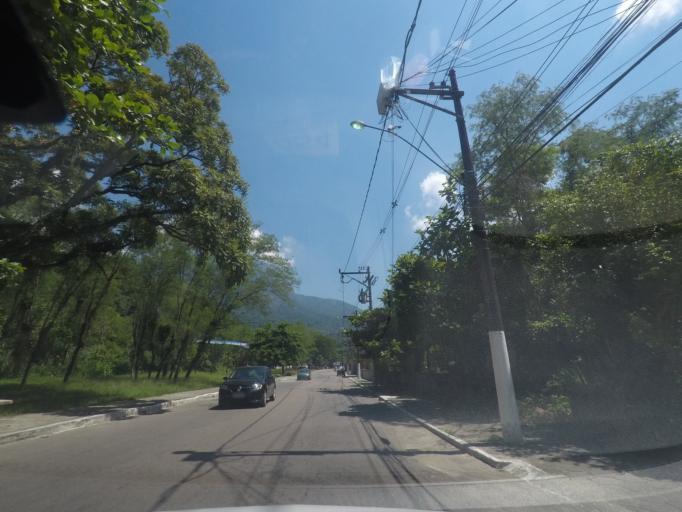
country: BR
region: Rio de Janeiro
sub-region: Petropolis
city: Petropolis
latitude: -22.5747
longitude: -43.1851
